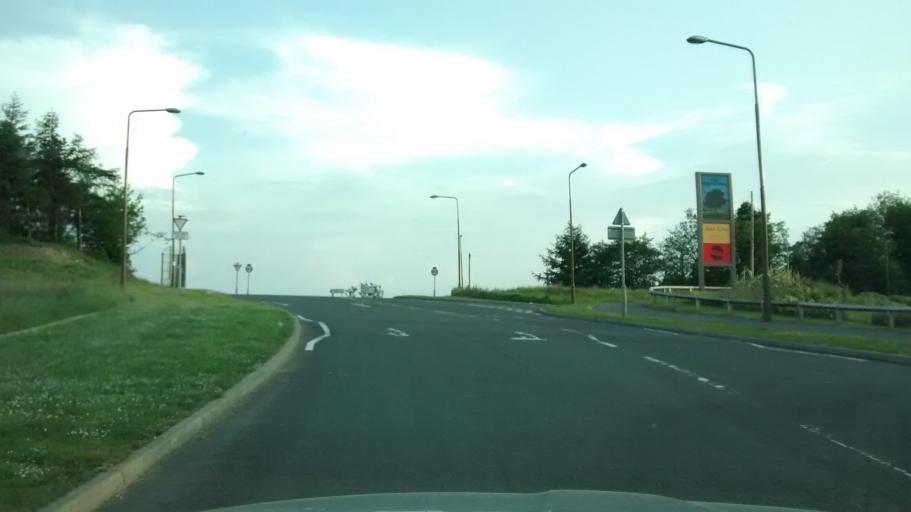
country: GB
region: Scotland
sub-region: West Lothian
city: Armadale
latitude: 55.8848
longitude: -3.6920
